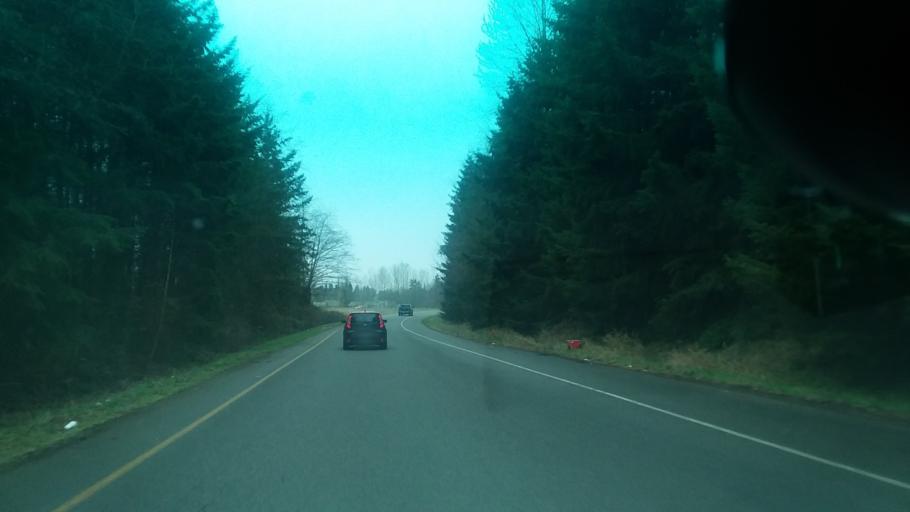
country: US
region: Washington
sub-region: Pierce County
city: Puyallup
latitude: 47.1600
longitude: -122.3070
